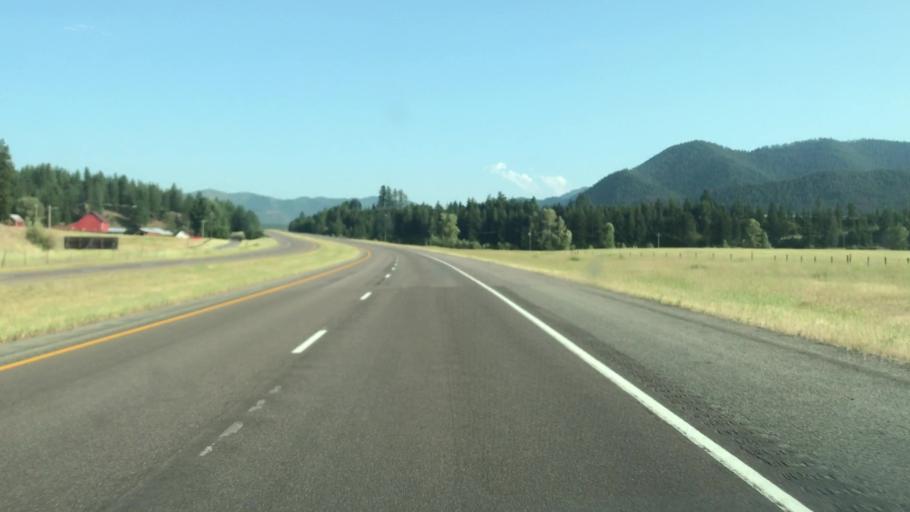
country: US
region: Montana
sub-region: Mineral County
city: Superior
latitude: 47.0579
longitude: -114.7624
